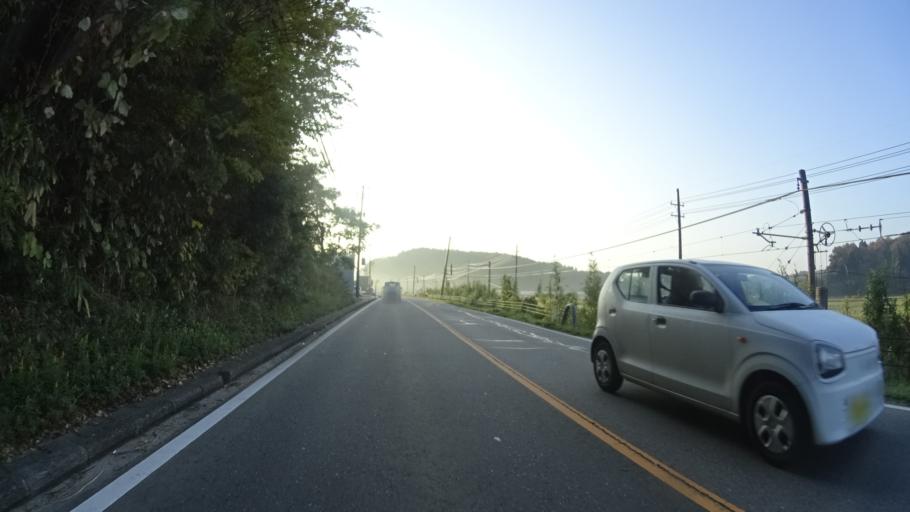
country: JP
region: Ishikawa
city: Nanao
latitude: 37.0701
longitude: 136.9324
